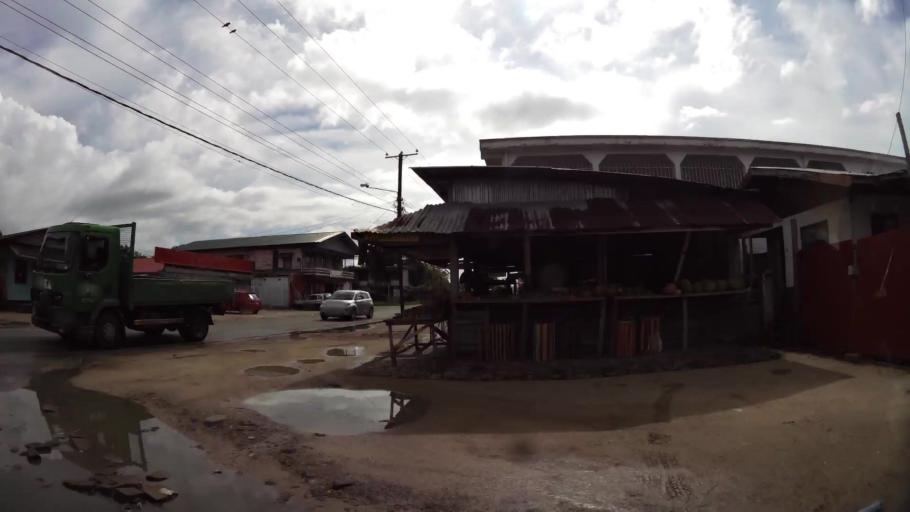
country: SR
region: Paramaribo
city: Paramaribo
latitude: 5.8427
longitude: -55.2085
